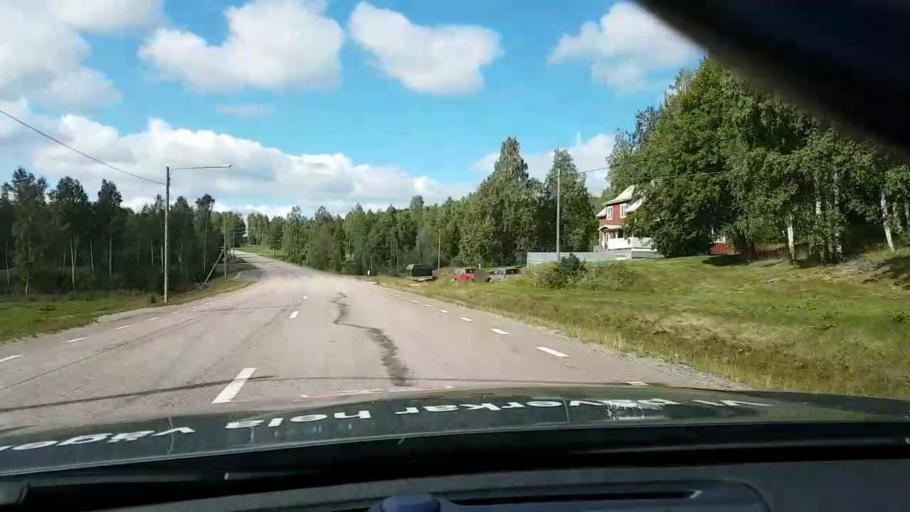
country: SE
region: Vaesternorrland
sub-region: OErnskoeldsviks Kommun
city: Bjasta
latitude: 63.3883
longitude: 18.3652
